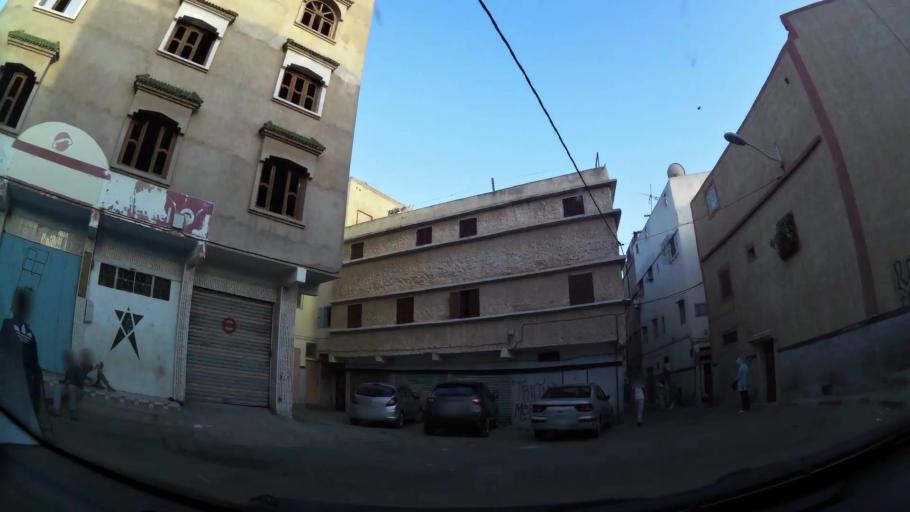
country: MA
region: Oued ed Dahab-Lagouira
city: Dakhla
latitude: 30.3886
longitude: -9.5688
